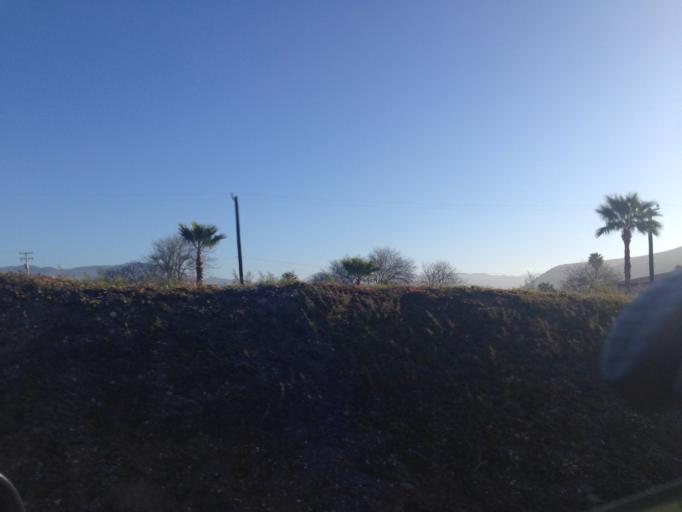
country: MX
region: Baja California
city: Primo Tapia
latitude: 32.2328
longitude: -116.9227
